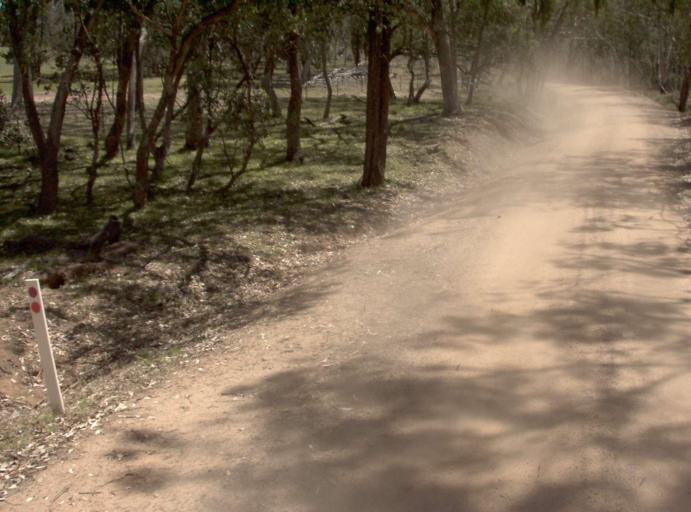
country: AU
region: New South Wales
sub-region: Snowy River
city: Jindabyne
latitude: -37.0895
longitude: 148.4331
